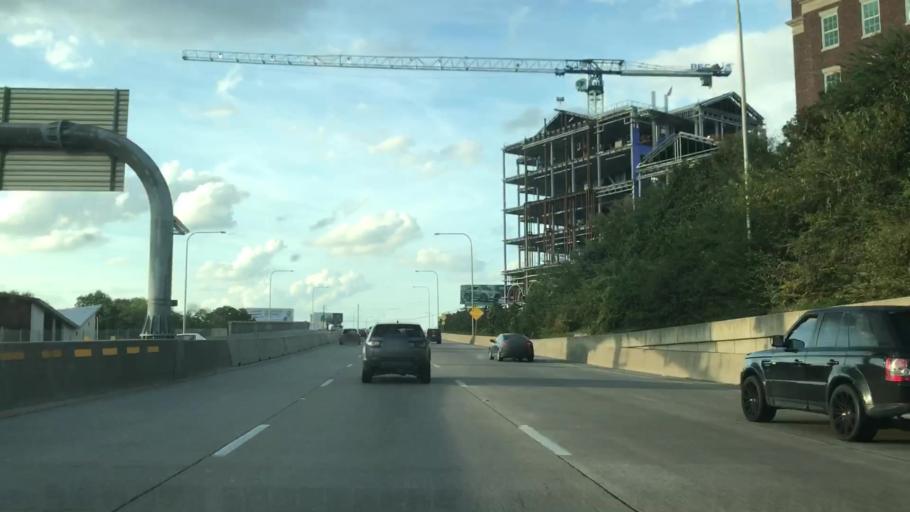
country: US
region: Texas
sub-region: Dallas County
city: Dallas
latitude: 32.8049
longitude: -96.8171
